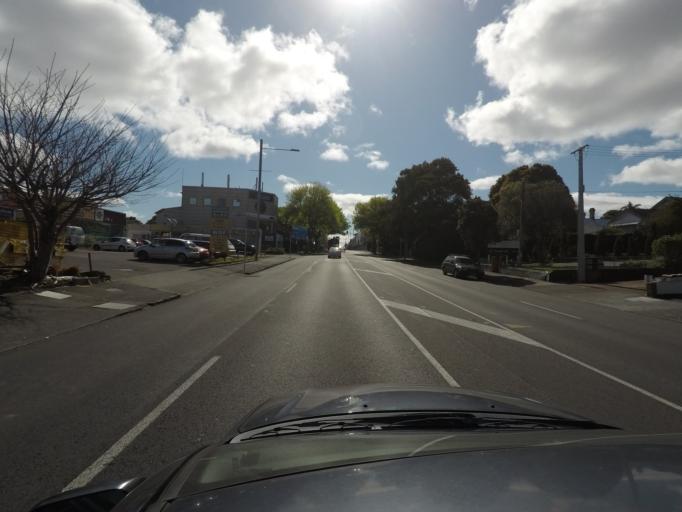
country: NZ
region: Auckland
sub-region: Auckland
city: Rosebank
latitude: -36.8864
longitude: 174.7132
